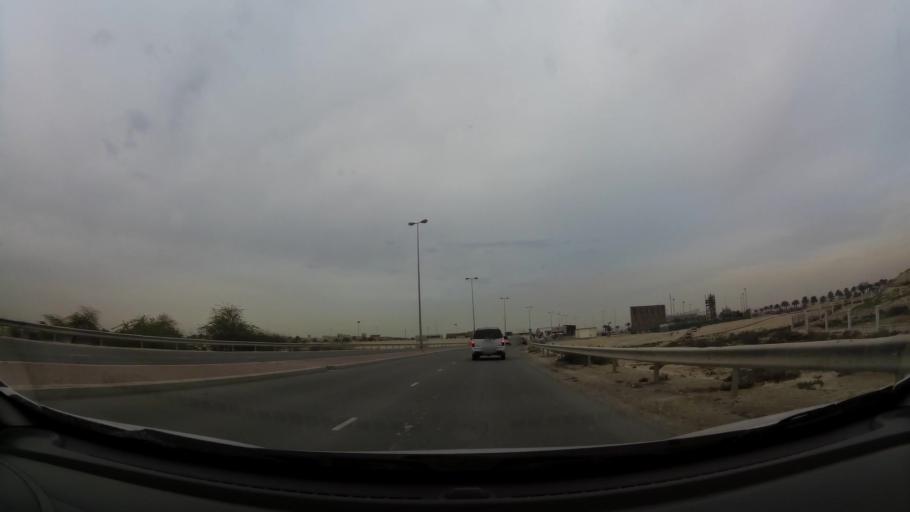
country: BH
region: Northern
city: Ar Rifa'
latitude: 26.0988
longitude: 50.5546
